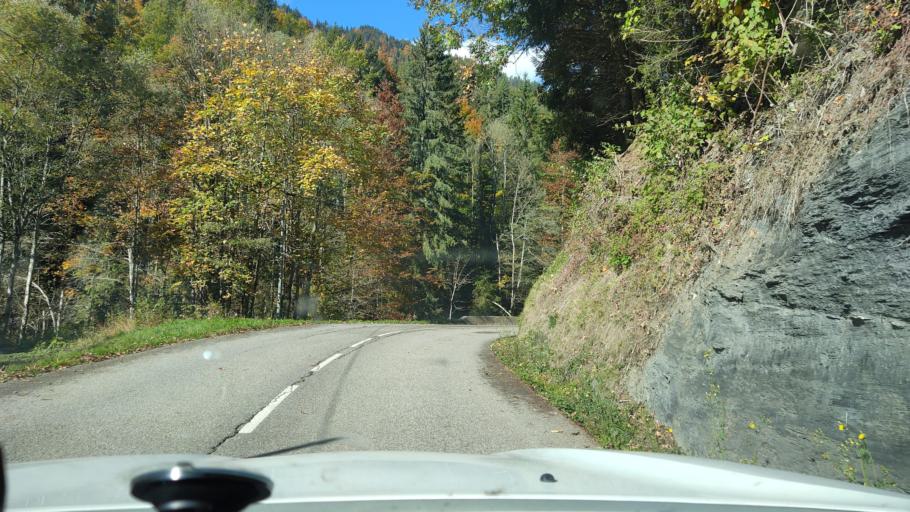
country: FR
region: Rhone-Alpes
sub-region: Departement de la Haute-Savoie
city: Praz-sur-Arly
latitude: 45.8399
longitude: 6.5073
